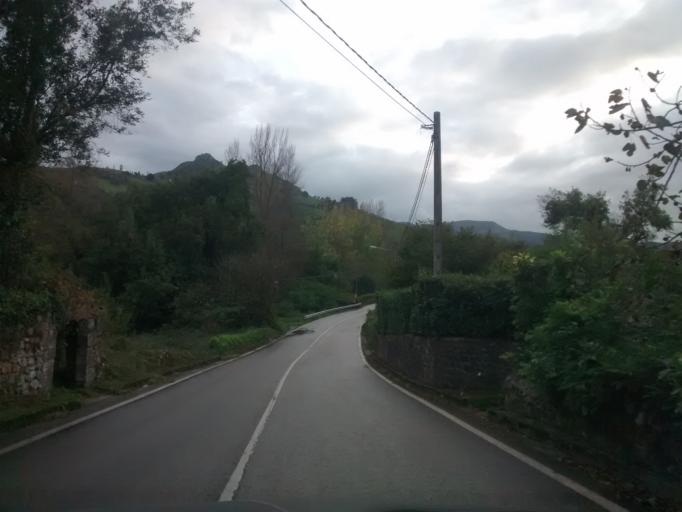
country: ES
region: Cantabria
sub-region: Provincia de Cantabria
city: Lierganes
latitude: 43.3479
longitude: -3.7326
